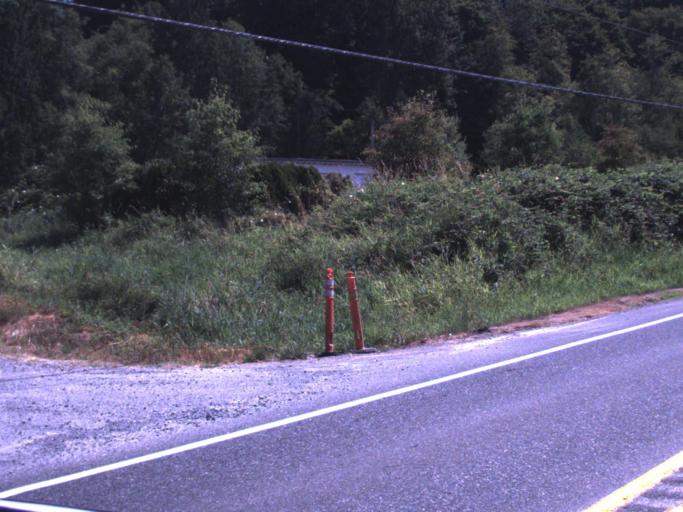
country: US
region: Washington
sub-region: King County
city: Ames Lake
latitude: 47.6206
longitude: -121.9605
